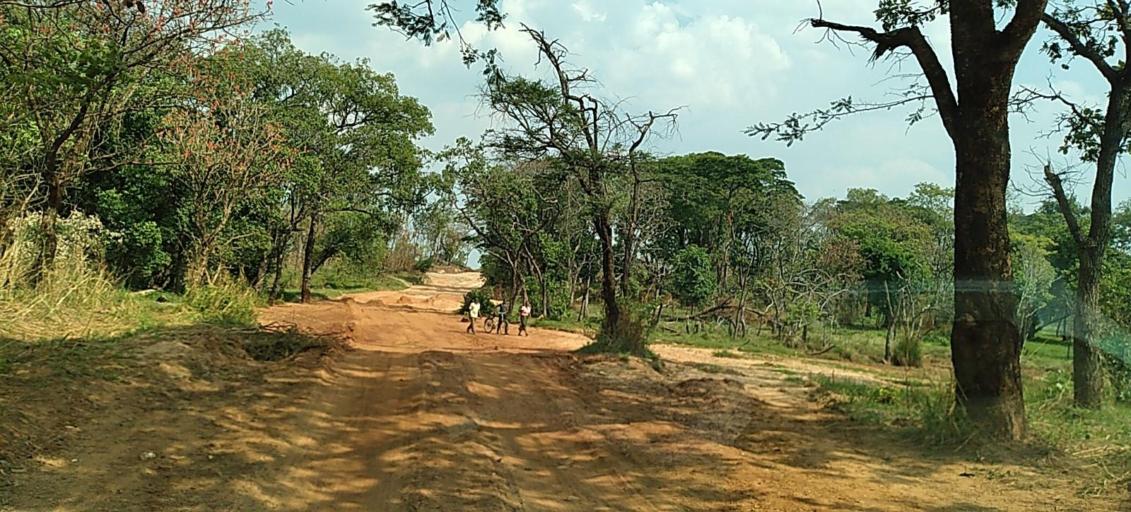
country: ZM
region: Copperbelt
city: Chingola
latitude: -12.7540
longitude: 27.7890
